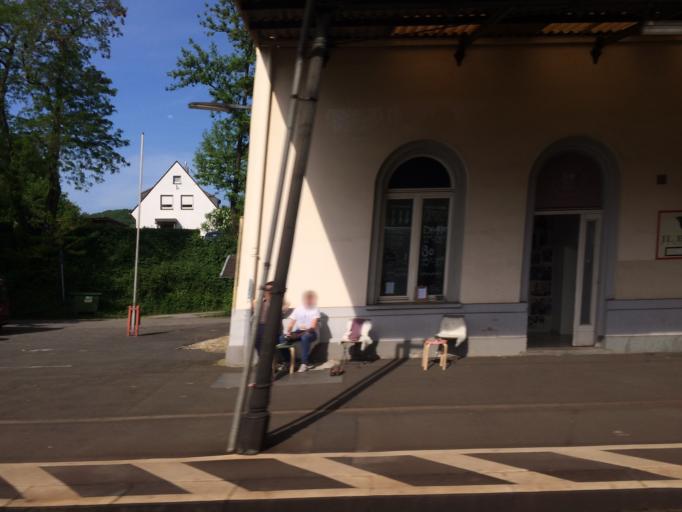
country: DE
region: North Rhine-Westphalia
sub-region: Regierungsbezirk Koln
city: Konigswinter
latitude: 50.7152
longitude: 7.1590
